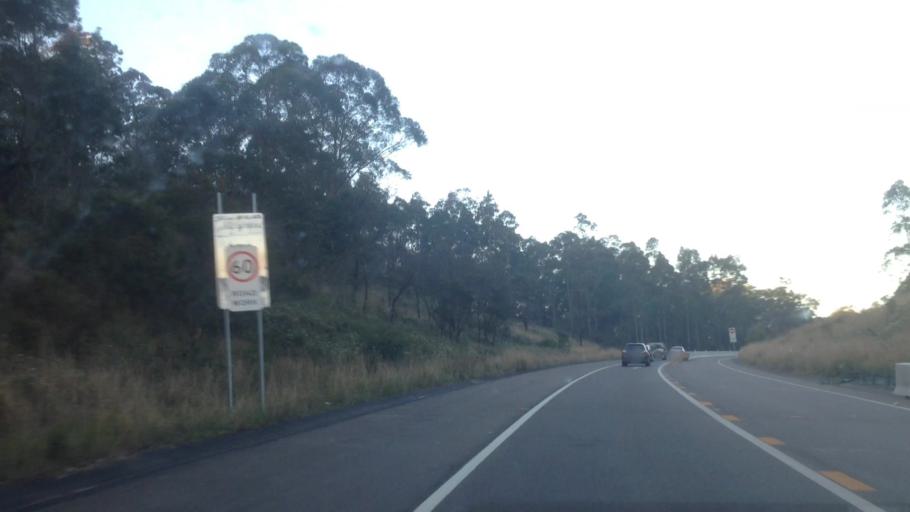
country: AU
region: New South Wales
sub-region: Wyong Shire
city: Jilliby
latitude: -33.2172
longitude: 151.4413
